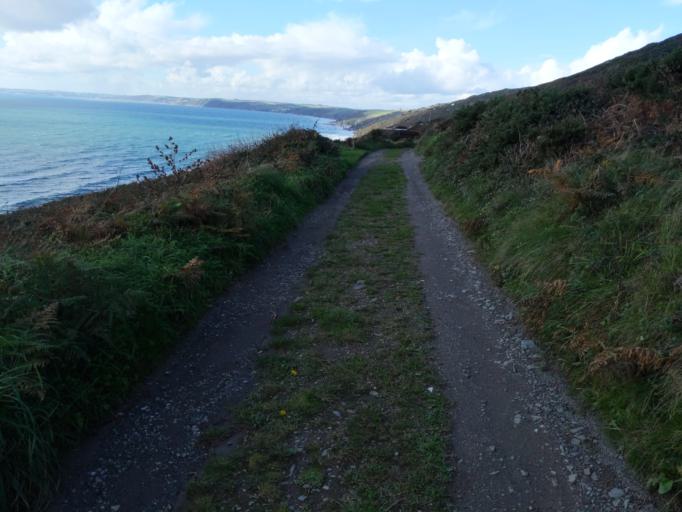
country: GB
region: England
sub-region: Cornwall
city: Torpoint
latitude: 50.3324
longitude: -4.2251
